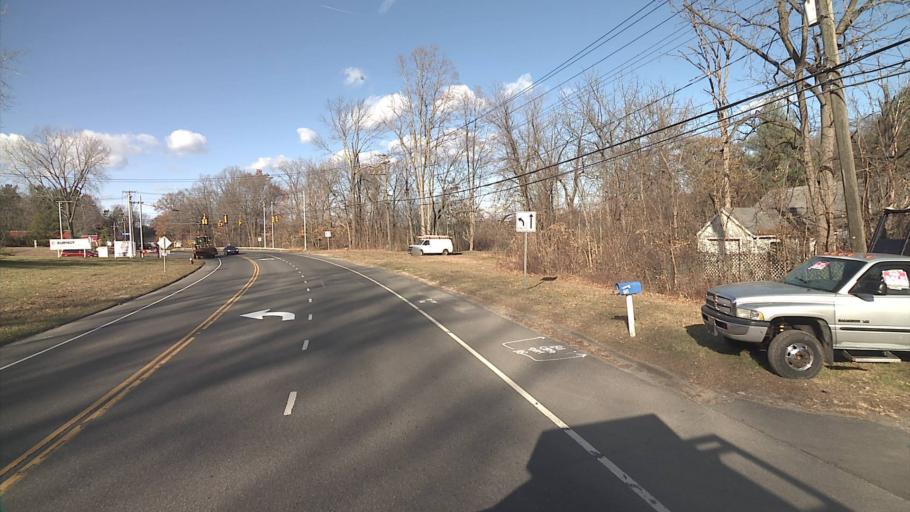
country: US
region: Connecticut
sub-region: Fairfield County
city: Bethel
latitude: 41.3594
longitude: -73.4191
